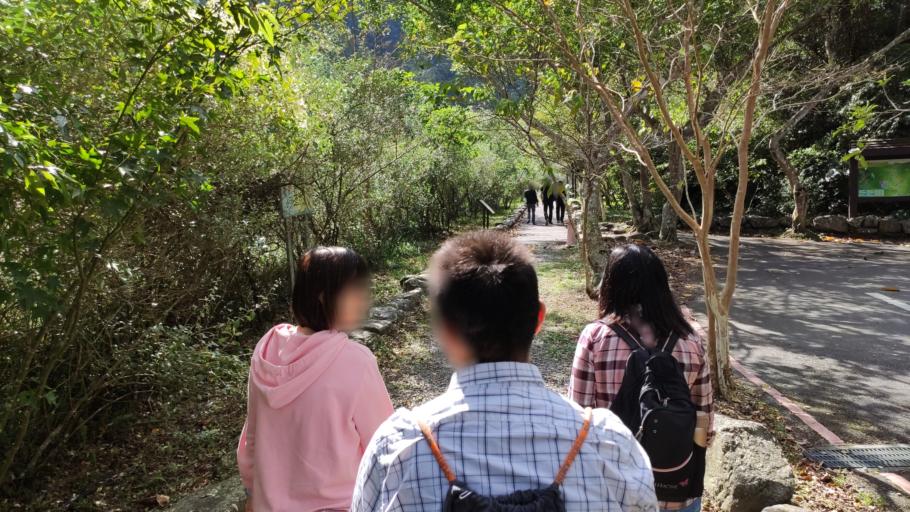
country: TW
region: Taiwan
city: Daxi
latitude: 24.8328
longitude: 121.4462
